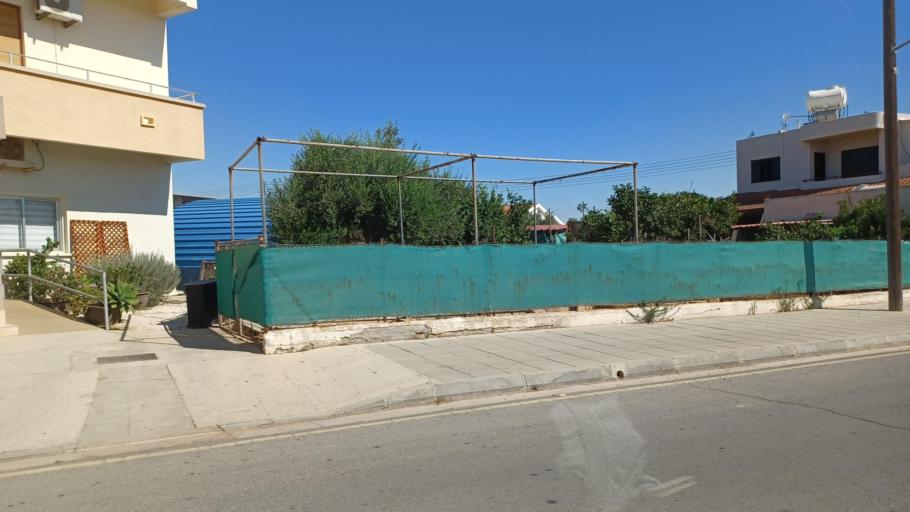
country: CY
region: Larnaka
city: Xylotymbou
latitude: 35.0219
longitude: 33.7478
